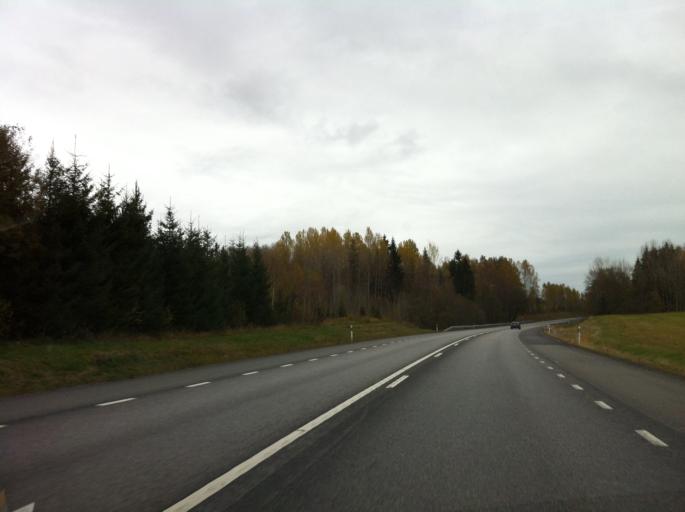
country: SE
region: OErebro
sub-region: Lindesbergs Kommun
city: Stora
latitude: 59.7382
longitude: 15.1360
